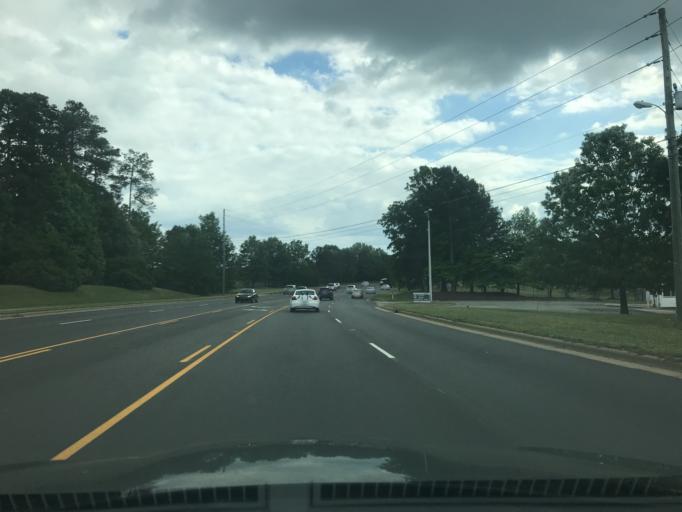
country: US
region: North Carolina
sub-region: Wake County
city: Wake Forest
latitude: 35.9144
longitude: -78.5952
